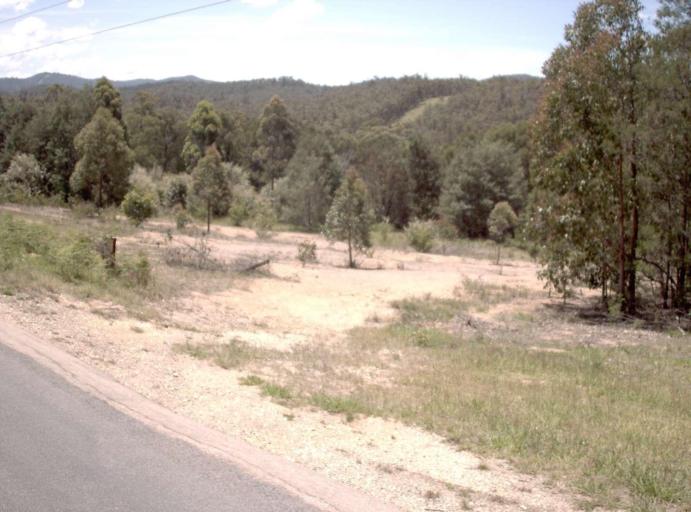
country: AU
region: New South Wales
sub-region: Bombala
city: Bombala
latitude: -37.5488
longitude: 148.9372
